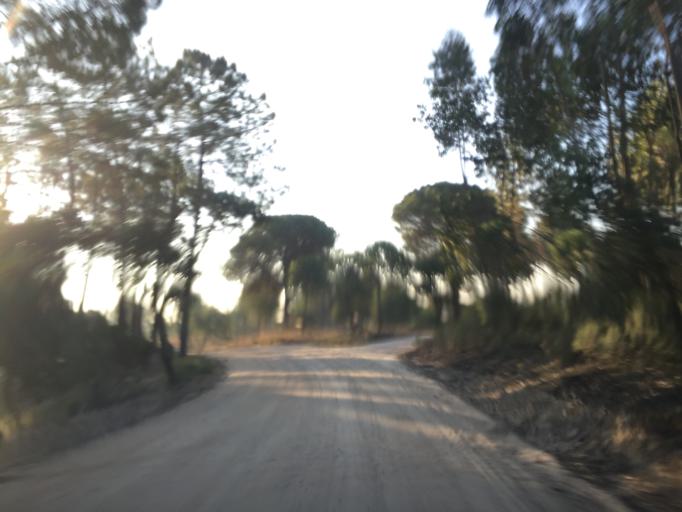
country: PT
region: Portalegre
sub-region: Ponte de Sor
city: Santo Andre
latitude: 39.0916
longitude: -8.3646
